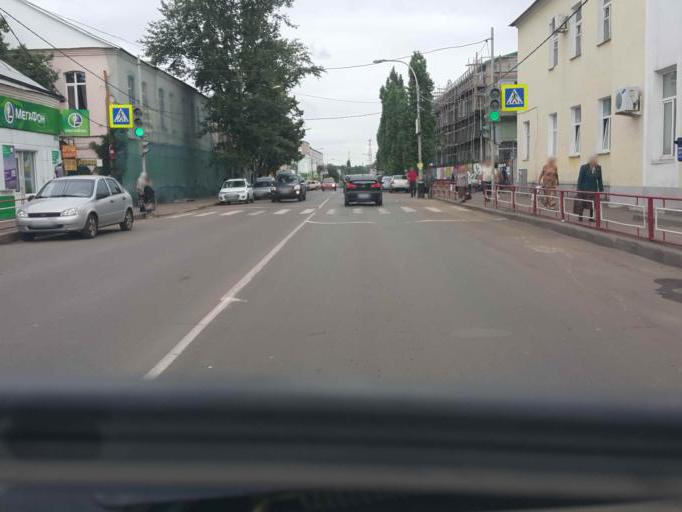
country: RU
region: Tambov
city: Michurinsk
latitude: 52.8873
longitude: 40.5122
